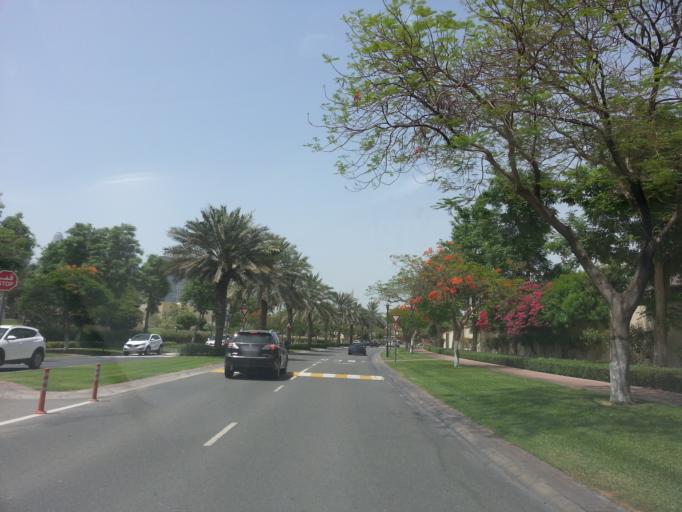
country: AE
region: Dubai
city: Dubai
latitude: 25.0678
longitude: 55.1548
